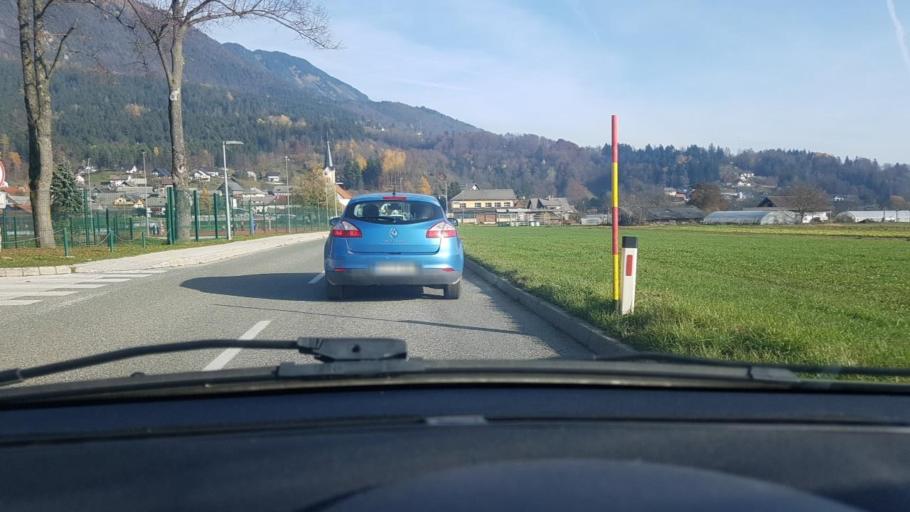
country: SI
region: Trzic
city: Bistrica pri Trzicu
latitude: 46.3393
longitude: 14.2948
